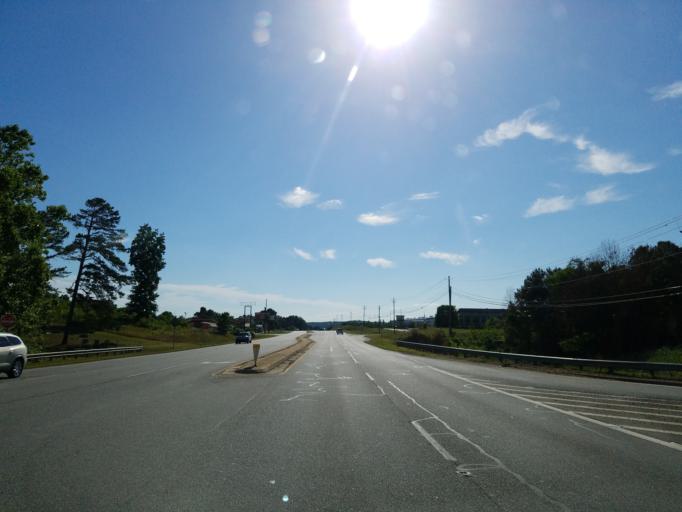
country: US
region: Georgia
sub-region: Bartow County
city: Adairsville
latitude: 34.3770
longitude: -84.9164
